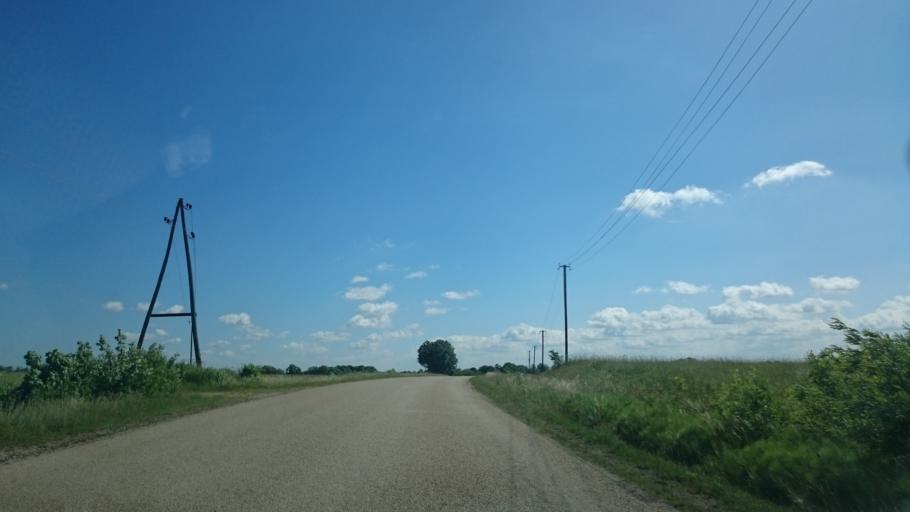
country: LV
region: Cibla
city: Cibla
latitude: 56.5345
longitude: 27.8529
